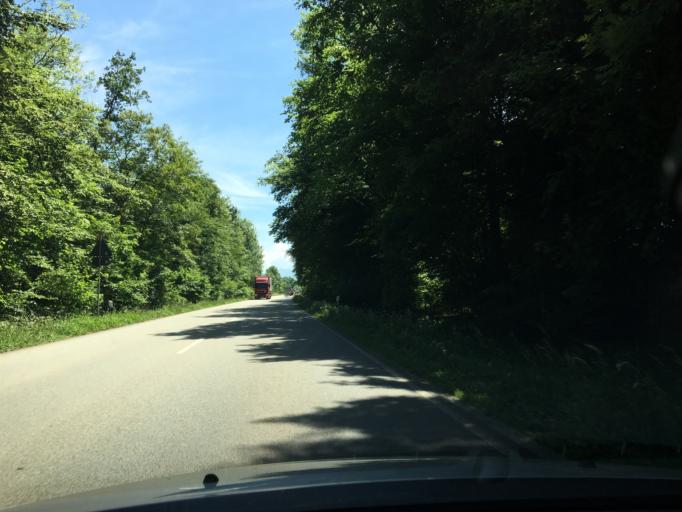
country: DE
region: Bavaria
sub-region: Upper Bavaria
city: Freilassing
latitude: 47.8699
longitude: 12.9759
